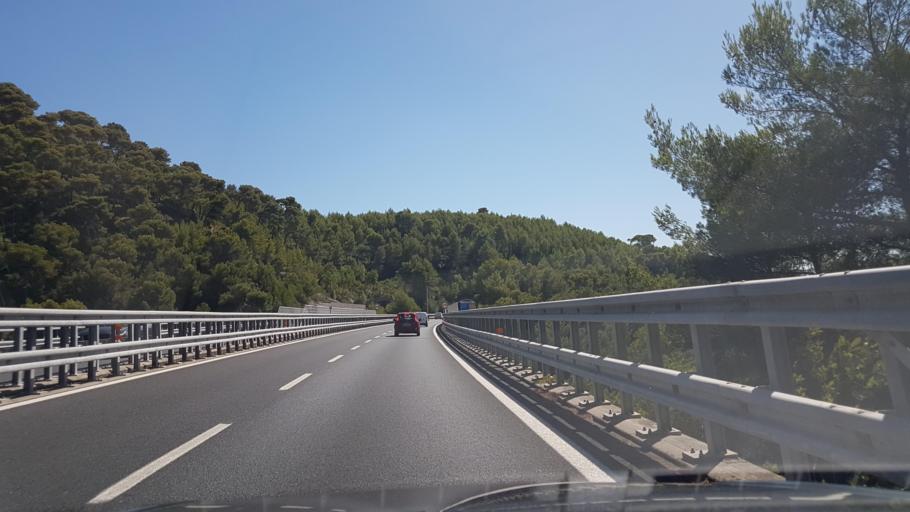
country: IT
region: Liguria
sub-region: Provincia di Savona
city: Laigueglia
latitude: 43.9811
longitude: 8.1382
